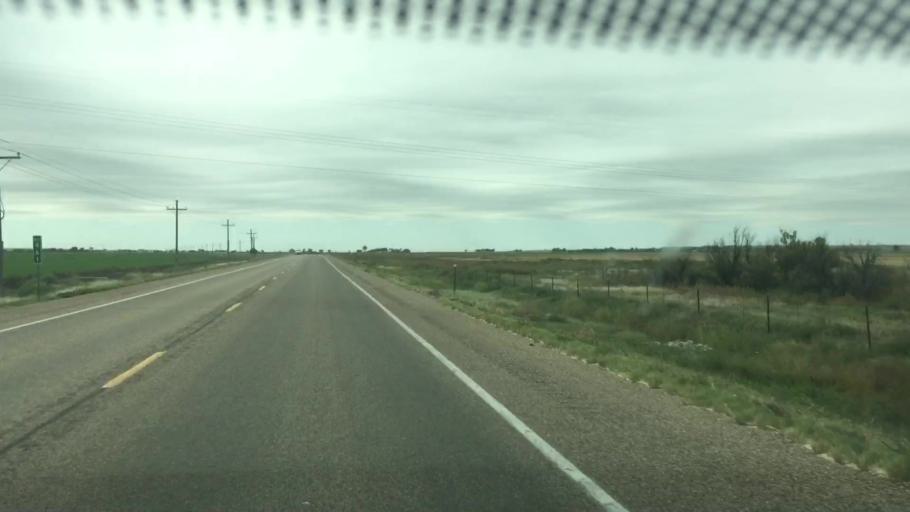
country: US
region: Kansas
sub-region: Hamilton County
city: Syracuse
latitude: 38.0566
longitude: -102.1640
